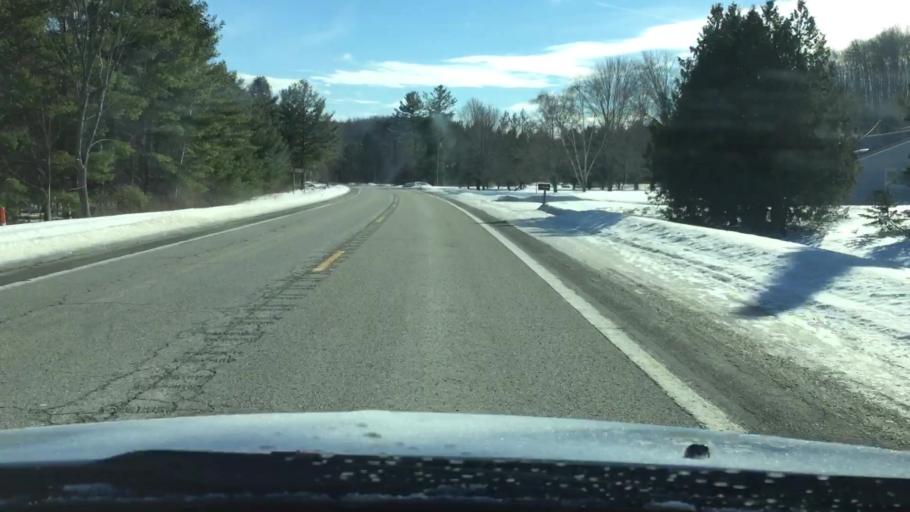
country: US
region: Michigan
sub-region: Charlevoix County
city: East Jordan
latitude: 45.1116
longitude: -85.1289
